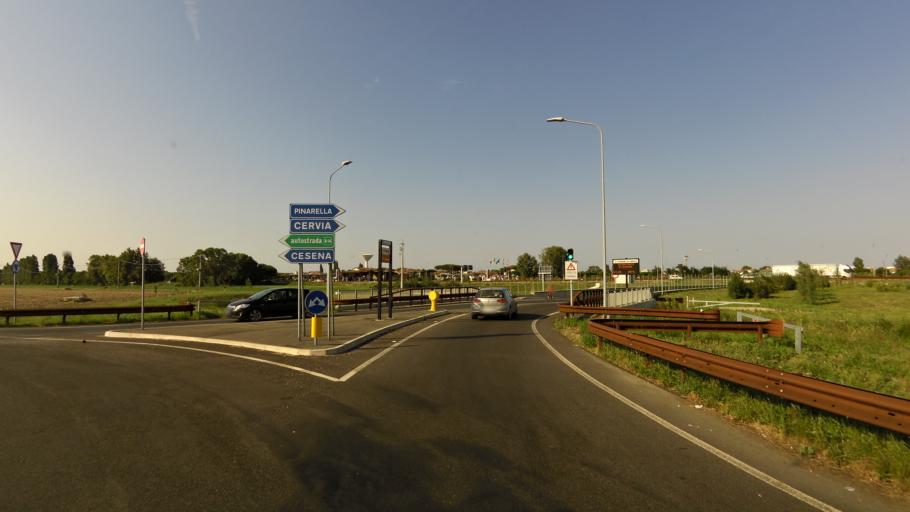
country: IT
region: Emilia-Romagna
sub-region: Provincia di Ravenna
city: Cervia
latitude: 44.2324
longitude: 12.3591
